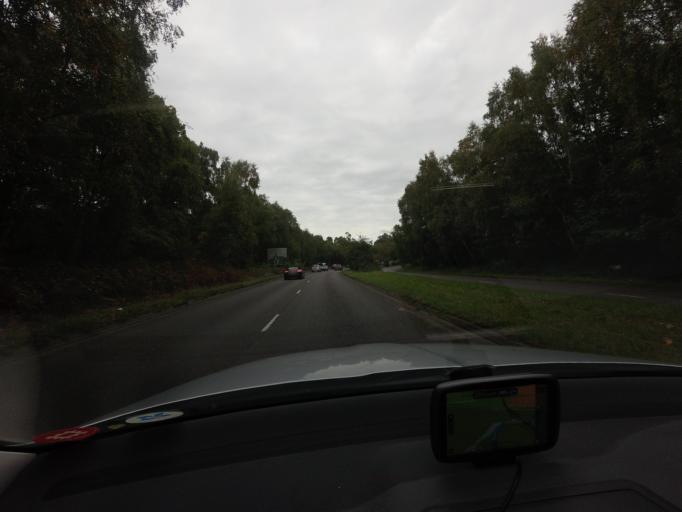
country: GB
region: England
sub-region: Surrey
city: Cobham
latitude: 51.3360
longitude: -0.4310
